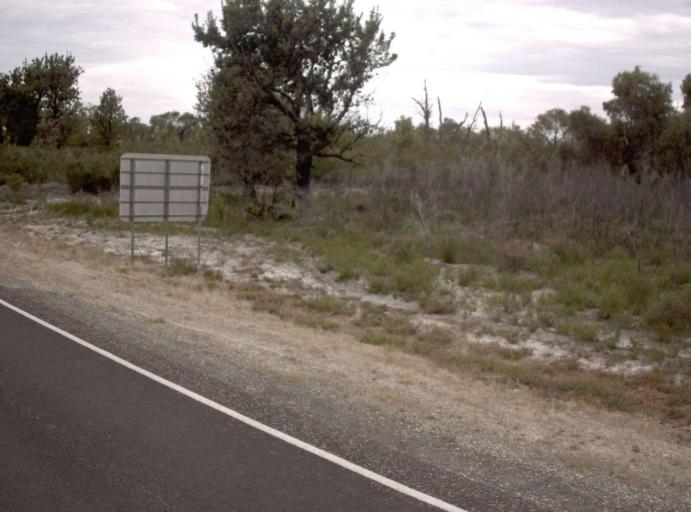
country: AU
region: Victoria
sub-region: Wellington
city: Sale
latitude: -38.1970
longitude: 147.3602
